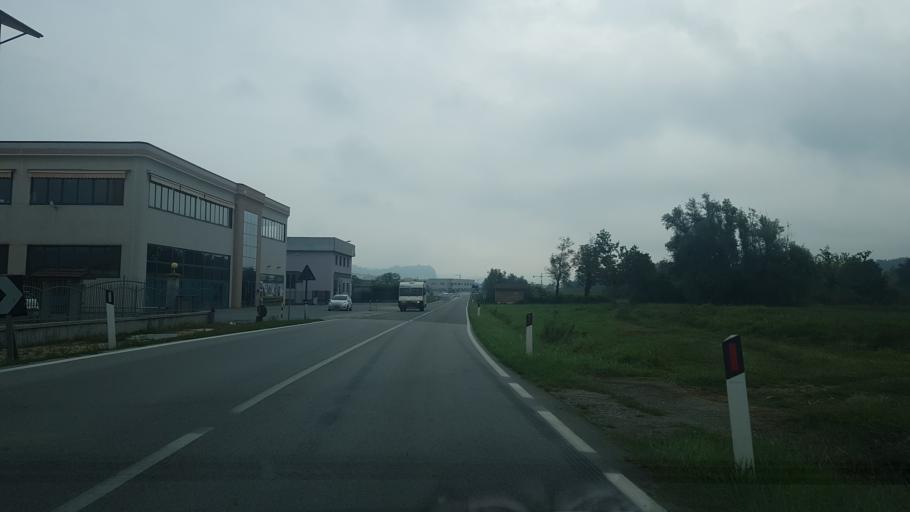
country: IT
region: Piedmont
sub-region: Provincia di Cuneo
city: Lesegno
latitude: 44.3981
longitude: 7.9836
